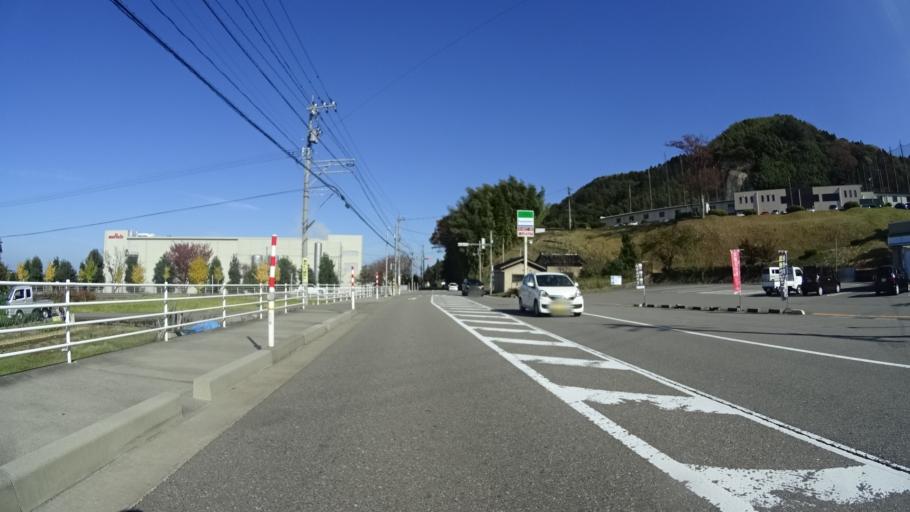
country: JP
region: Ishikawa
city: Tsurugi-asahimachi
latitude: 36.4903
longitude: 136.6191
